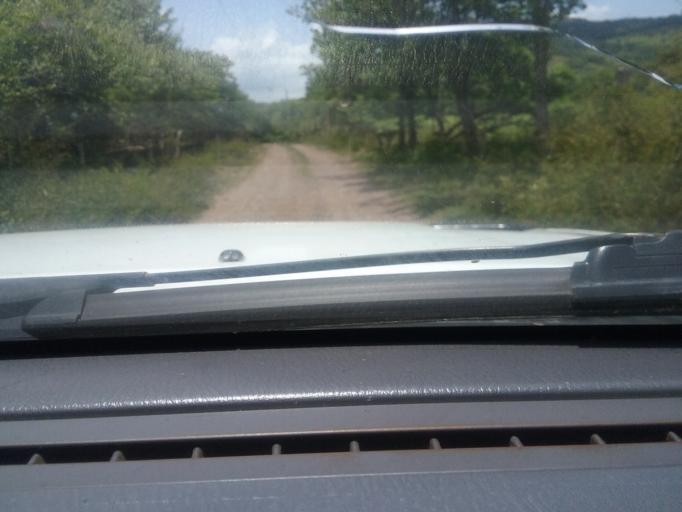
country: NI
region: Matagalpa
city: Terrabona
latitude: 12.6510
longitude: -85.9982
